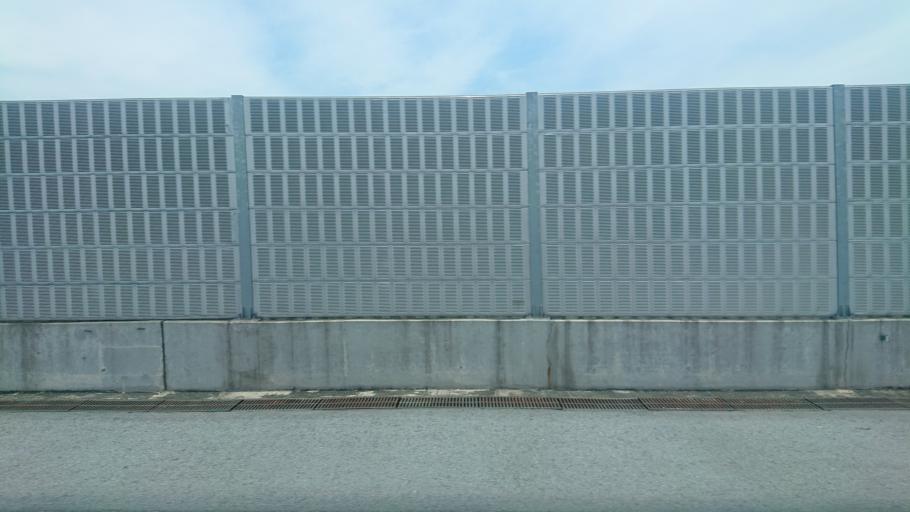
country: VN
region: Hai Duong
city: Tu Ky
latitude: 20.8361
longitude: 106.4328
